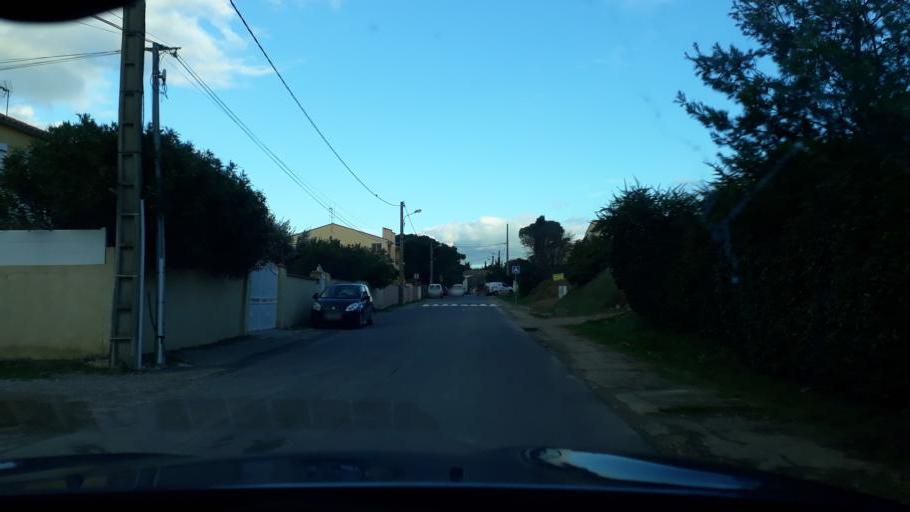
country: FR
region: Languedoc-Roussillon
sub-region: Departement de l'Herault
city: Nissan-lez-Enserune
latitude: 43.2849
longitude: 3.1338
